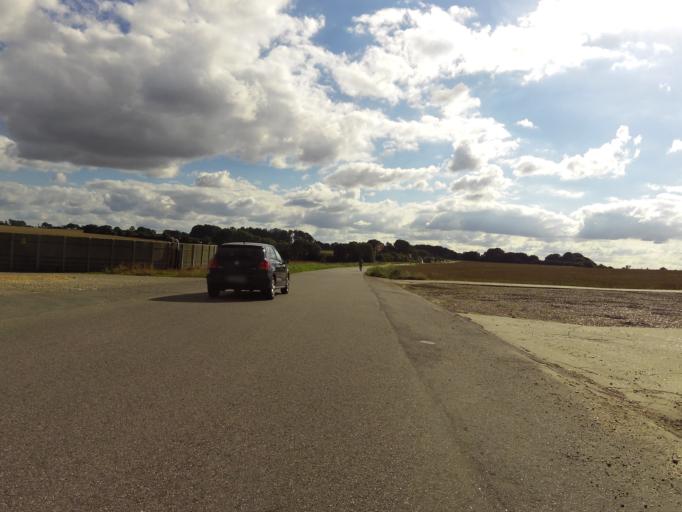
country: DK
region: South Denmark
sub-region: Haderslev Kommune
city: Haderslev
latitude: 55.2335
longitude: 9.4639
